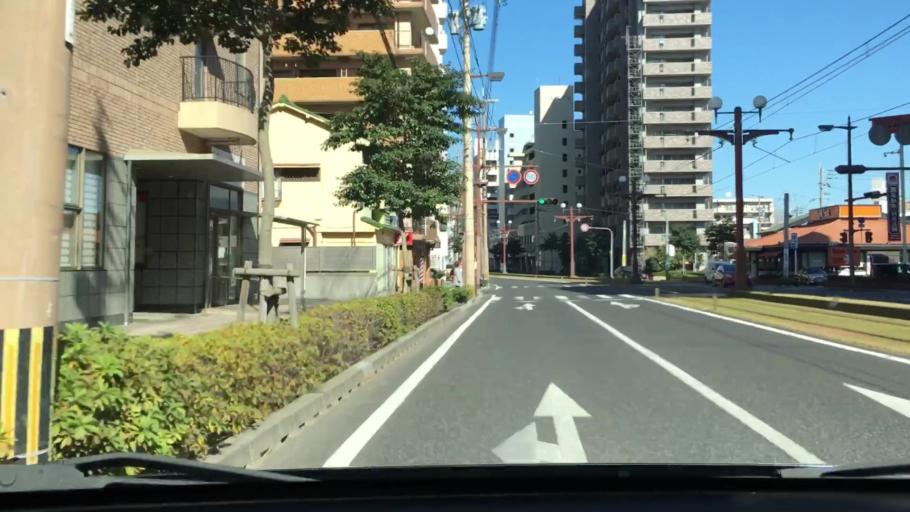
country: JP
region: Kagoshima
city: Kagoshima-shi
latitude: 31.5764
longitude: 130.5421
